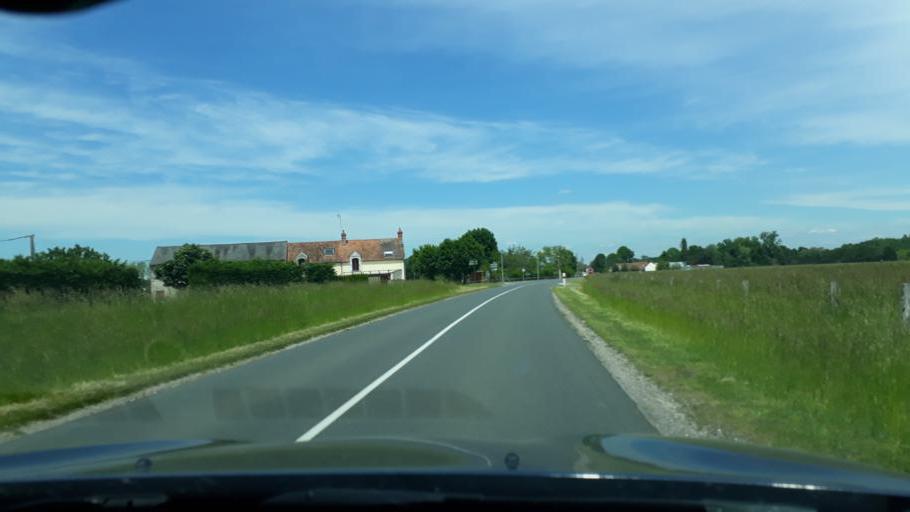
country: FR
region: Centre
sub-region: Departement du Loiret
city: Boiscommun
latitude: 48.0506
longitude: 2.2984
